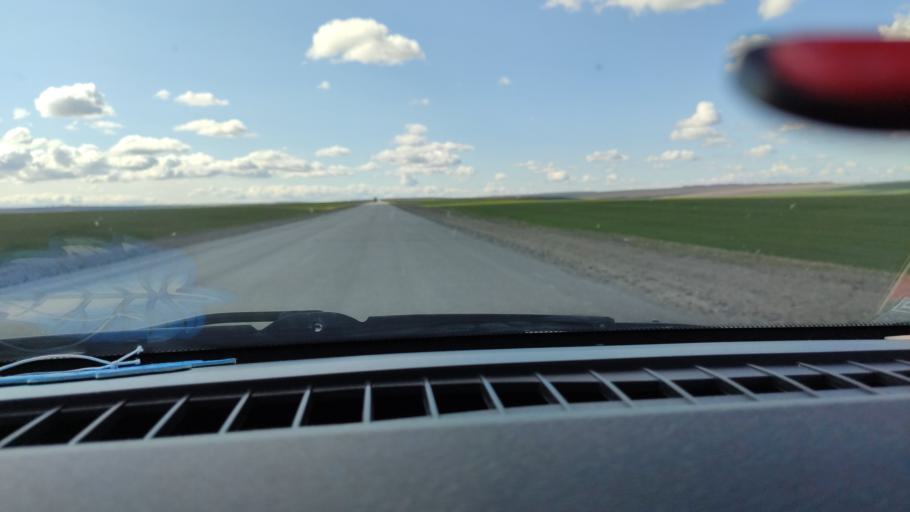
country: RU
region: Samara
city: Varlamovo
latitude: 53.0493
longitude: 48.3443
